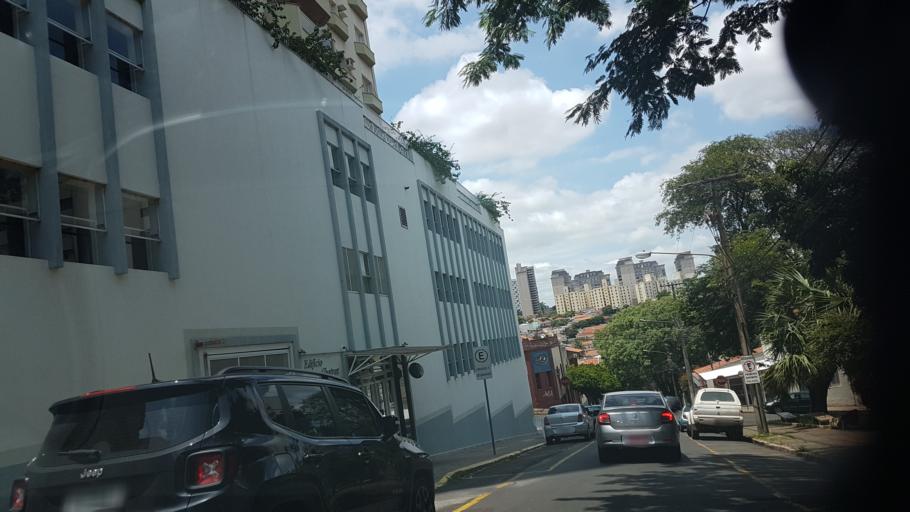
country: BR
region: Sao Paulo
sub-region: Piracicaba
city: Piracicaba
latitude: -22.7229
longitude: -47.6529
